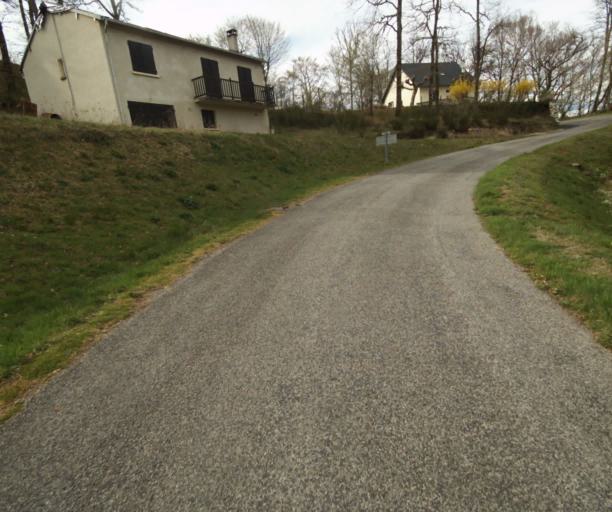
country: FR
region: Limousin
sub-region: Departement de la Correze
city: Argentat
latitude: 45.1973
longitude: 1.9726
